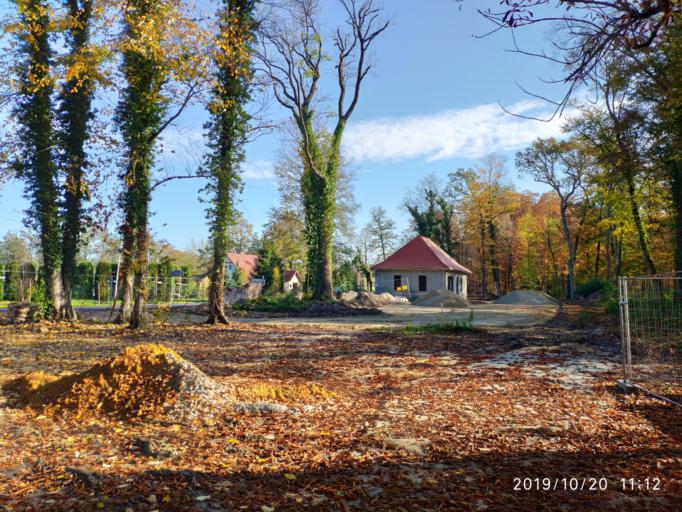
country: PL
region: Lubusz
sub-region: Zielona Gora
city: Zielona Gora
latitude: 51.8616
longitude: 15.5645
